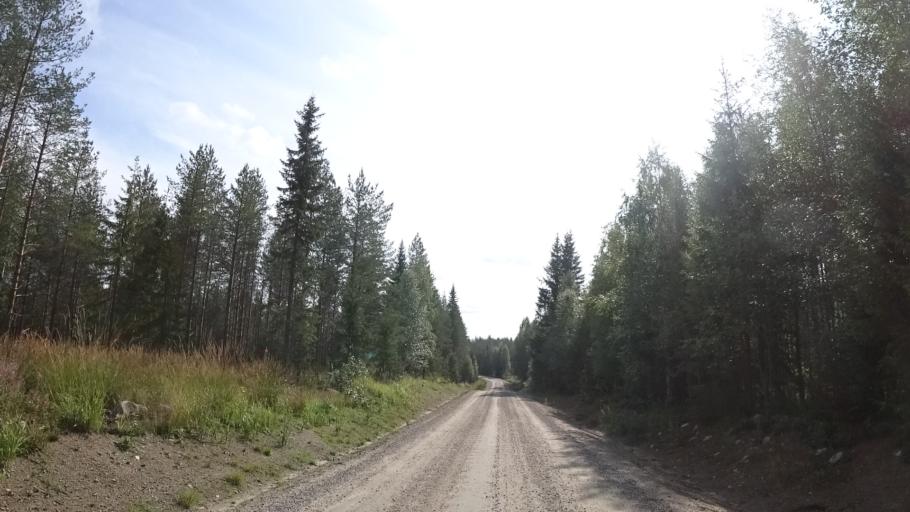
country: FI
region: North Karelia
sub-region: Pielisen Karjala
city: Lieksa
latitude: 63.5932
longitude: 30.1377
